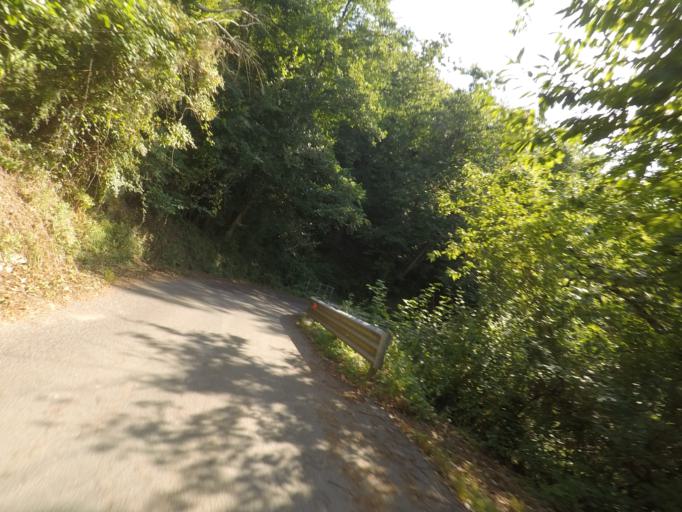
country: IT
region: Liguria
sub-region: Provincia di La Spezia
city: Casano-Dogana-Isola
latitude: 44.0857
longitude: 10.0619
